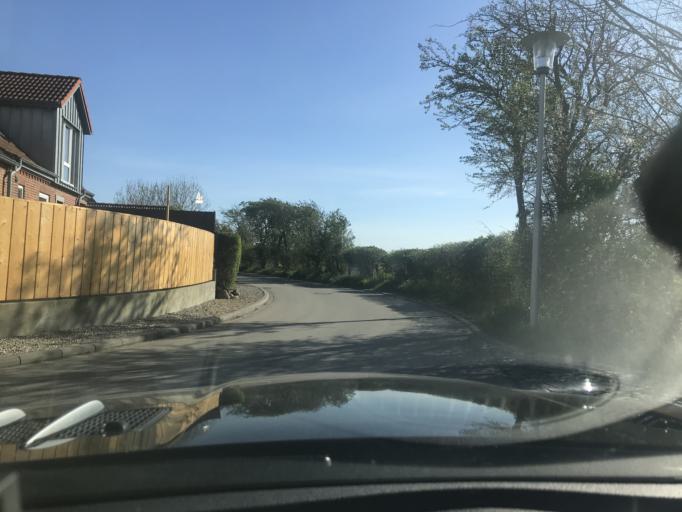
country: DE
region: Schleswig-Holstein
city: Grossenbrode
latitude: 54.4607
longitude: 11.0221
